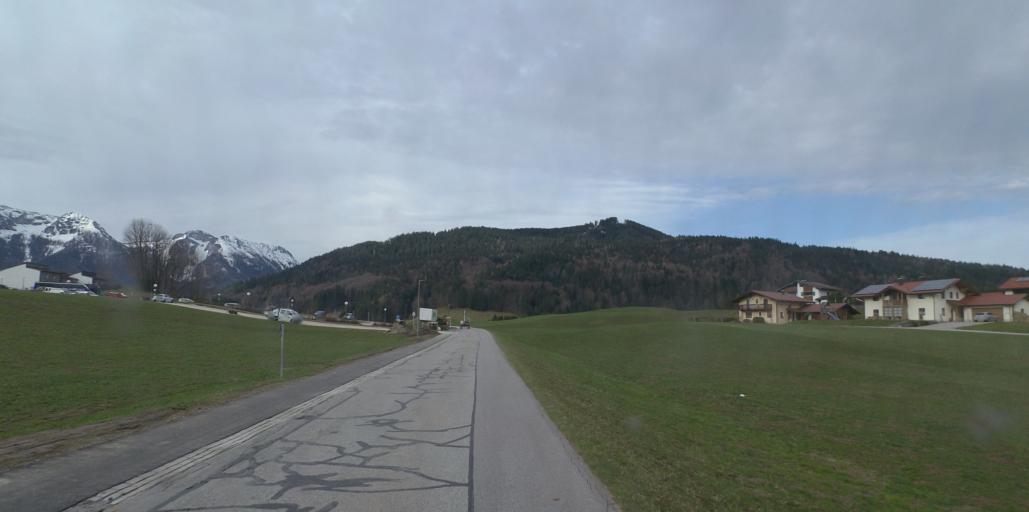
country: DE
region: Bavaria
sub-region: Upper Bavaria
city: Inzell
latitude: 47.7817
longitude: 12.7282
